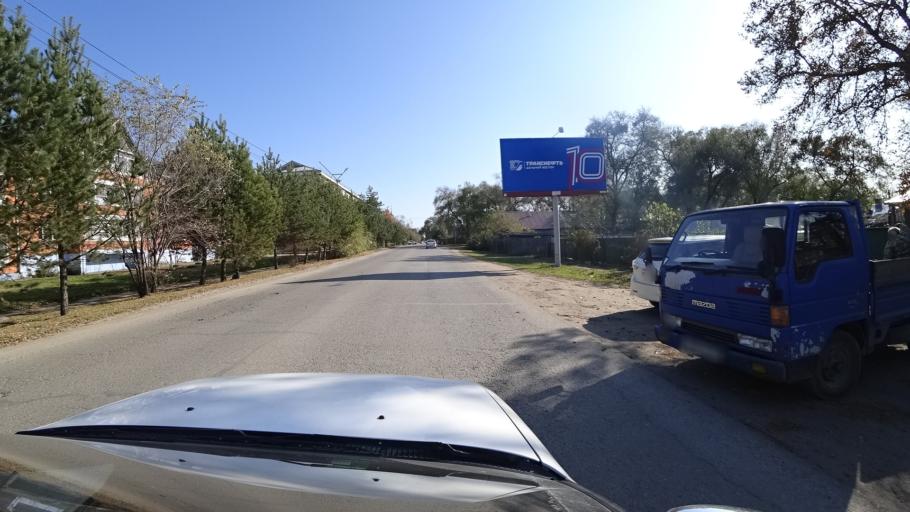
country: RU
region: Primorskiy
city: Dal'nerechensk
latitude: 45.9354
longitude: 133.7278
